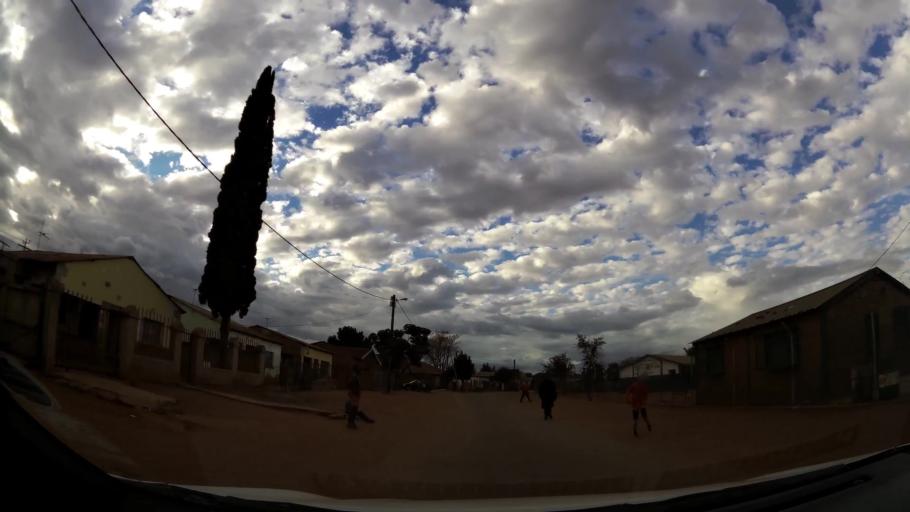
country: ZA
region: Limpopo
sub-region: Waterberg District Municipality
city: Modimolle
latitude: -24.5233
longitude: 28.7227
